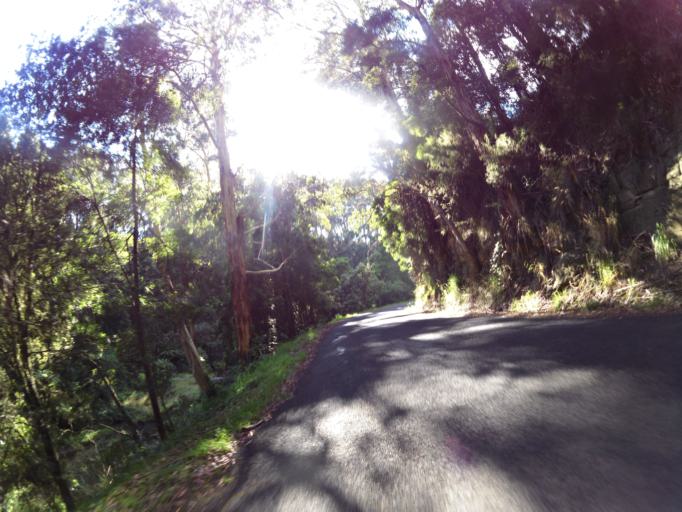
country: AU
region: Victoria
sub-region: Colac-Otway
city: Apollo Bay
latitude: -38.7573
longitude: 143.6254
